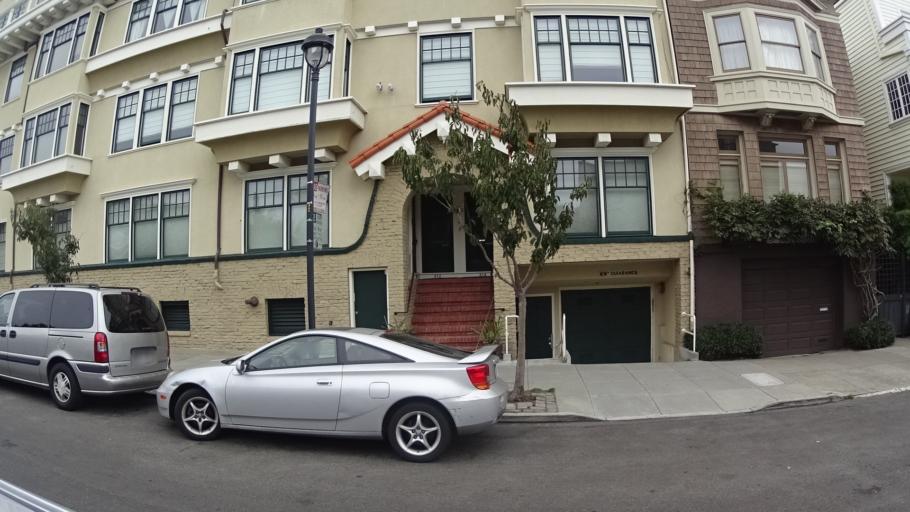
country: US
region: California
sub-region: San Francisco County
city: San Francisco
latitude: 37.7883
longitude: -122.4521
